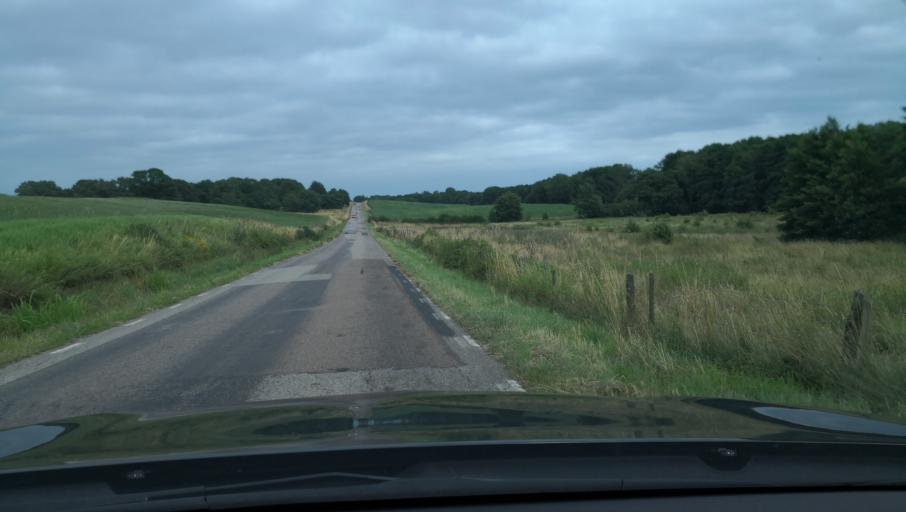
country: SE
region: Skane
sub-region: Simrishamns Kommun
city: Kivik
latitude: 55.6970
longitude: 14.1783
